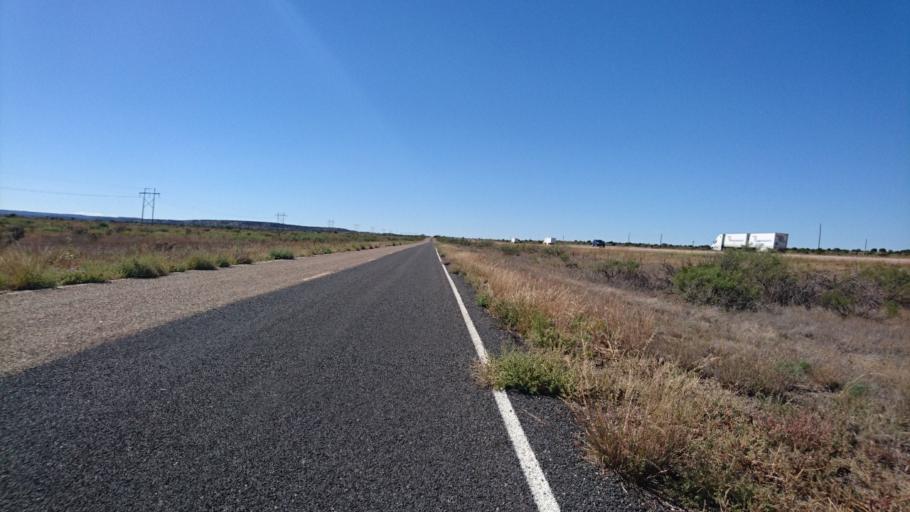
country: US
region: New Mexico
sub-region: Quay County
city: Tucumcari
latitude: 35.0753
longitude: -104.1416
